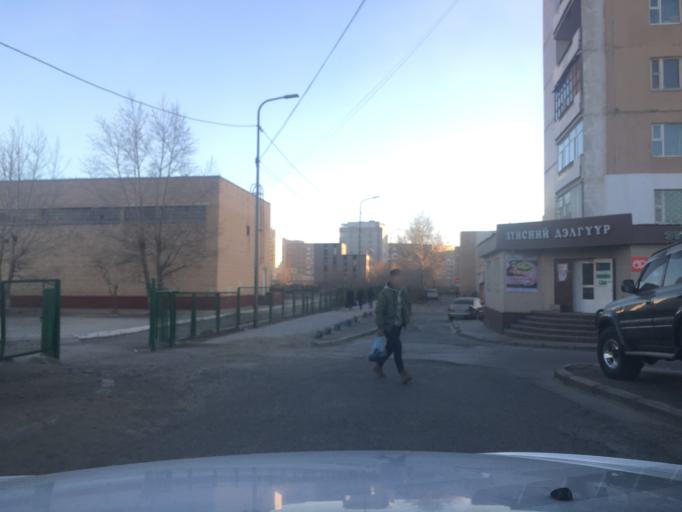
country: MN
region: Ulaanbaatar
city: Ulaanbaatar
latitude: 47.9154
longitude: 106.8334
